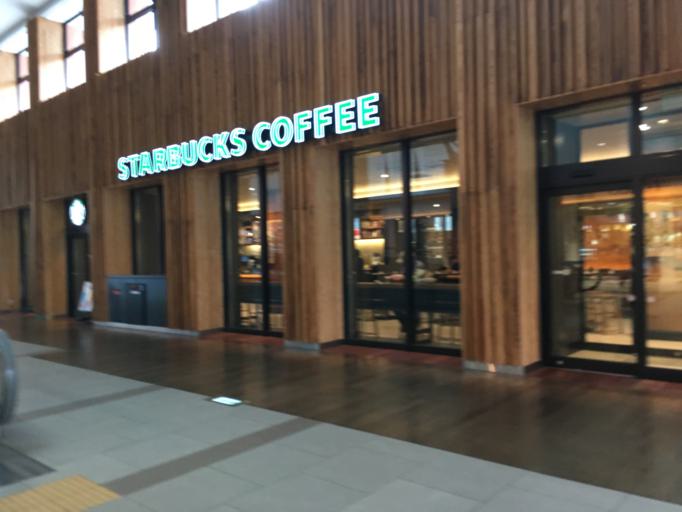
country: JP
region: Akita
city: Akita
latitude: 39.7167
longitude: 140.1293
